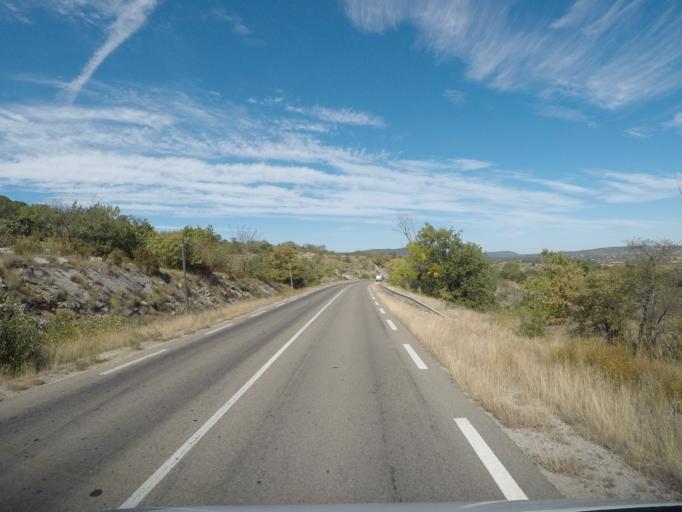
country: FR
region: Languedoc-Roussillon
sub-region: Departement de l'Herault
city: Saint-Martin-de-Londres
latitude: 43.8038
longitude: 3.7382
